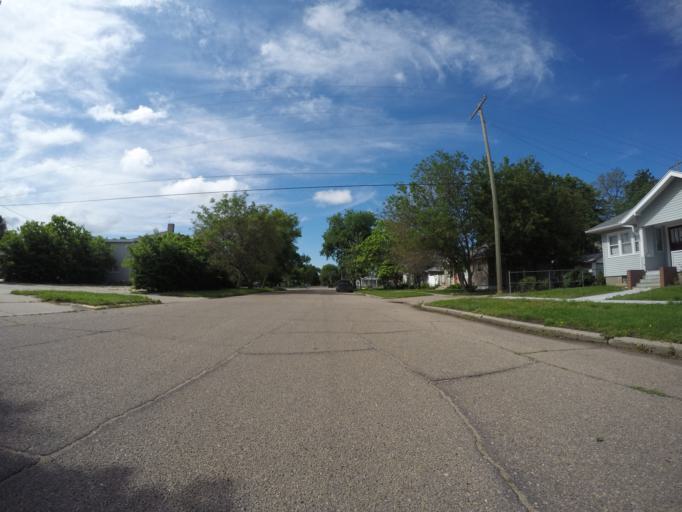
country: US
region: Nebraska
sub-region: Buffalo County
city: Kearney
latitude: 40.7013
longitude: -99.0898
